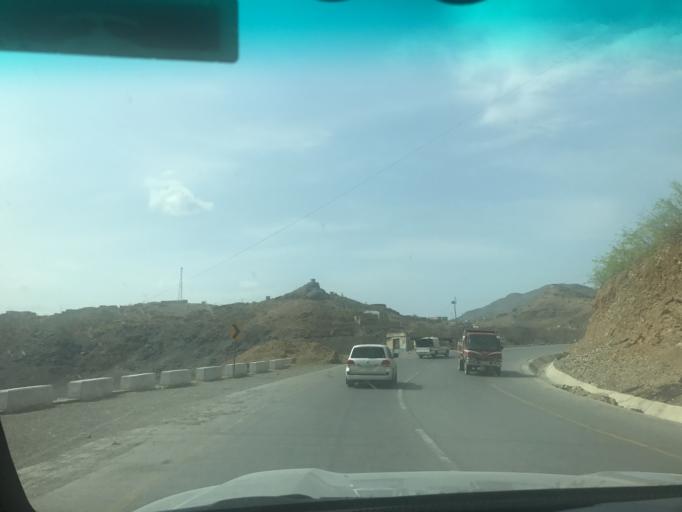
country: PK
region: Federally Administered Tribal Areas
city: Landi Kotal
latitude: 34.0233
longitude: 71.2643
